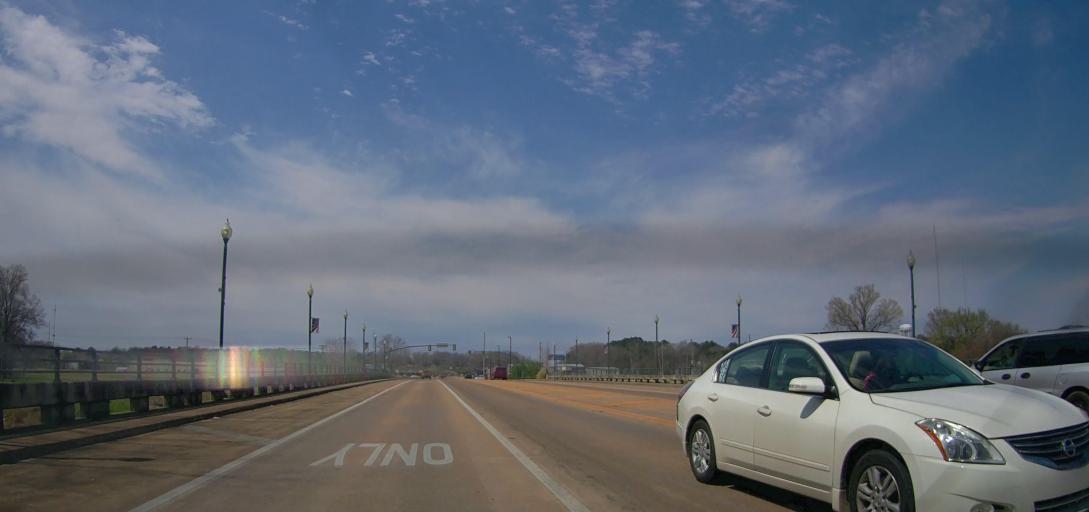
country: US
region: Mississippi
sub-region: Union County
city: New Albany
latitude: 34.4951
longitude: -89.0126
